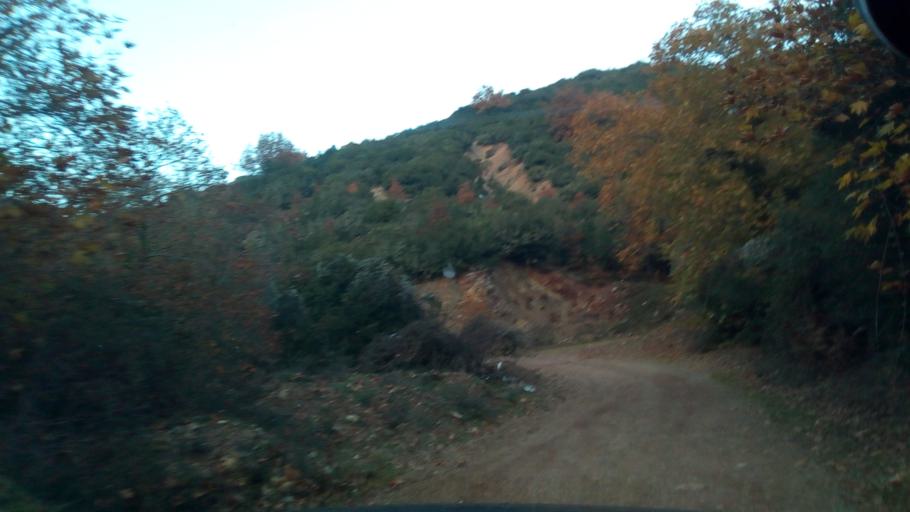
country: GR
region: West Greece
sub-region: Nomos Aitolias kai Akarnanias
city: Nafpaktos
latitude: 38.4704
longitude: 21.8138
